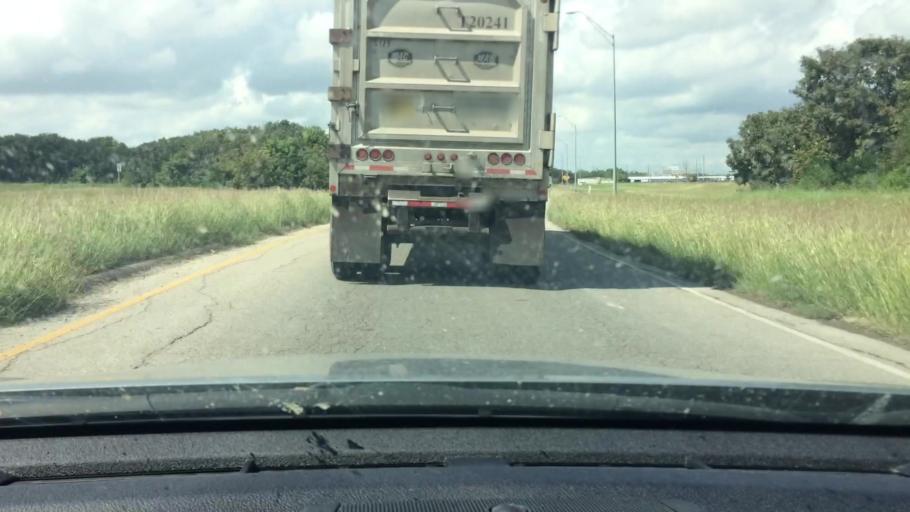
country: US
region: Texas
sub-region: Bexar County
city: Kirby
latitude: 29.4372
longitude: -98.3877
